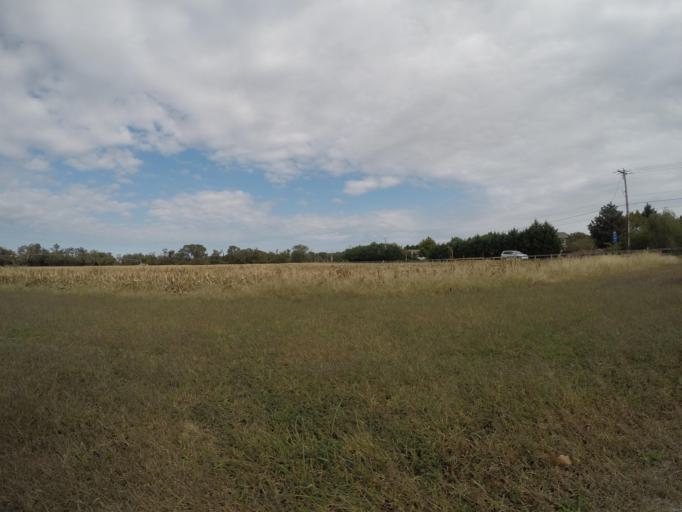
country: US
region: Delaware
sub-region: Sussex County
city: Rehoboth Beach
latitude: 38.7217
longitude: -75.1059
